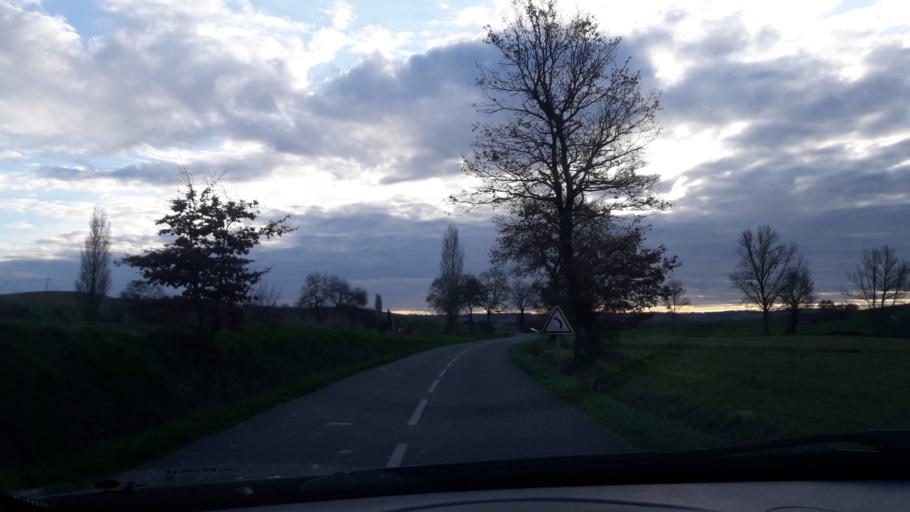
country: FR
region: Midi-Pyrenees
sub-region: Departement du Gers
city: Pujaudran
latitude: 43.6568
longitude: 1.1195
